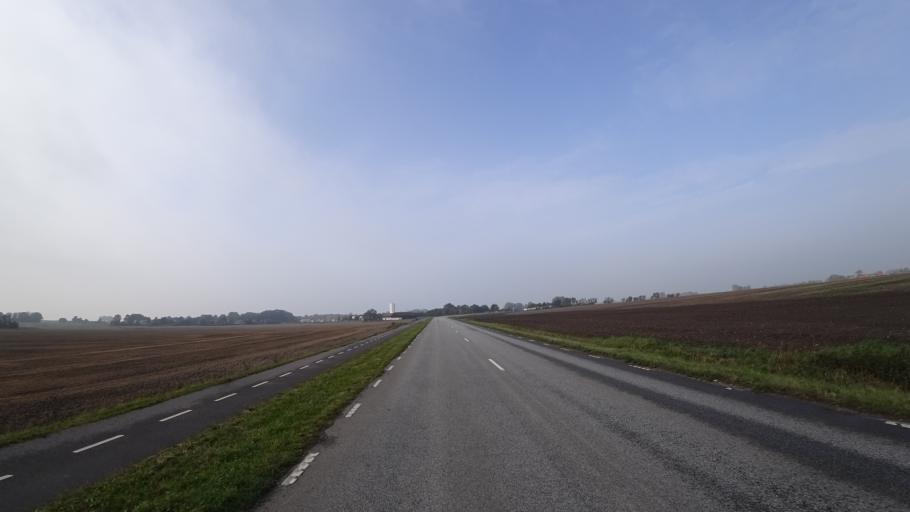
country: SE
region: Skane
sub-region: Kavlinge Kommun
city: Hofterup
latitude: 55.7688
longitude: 12.9699
